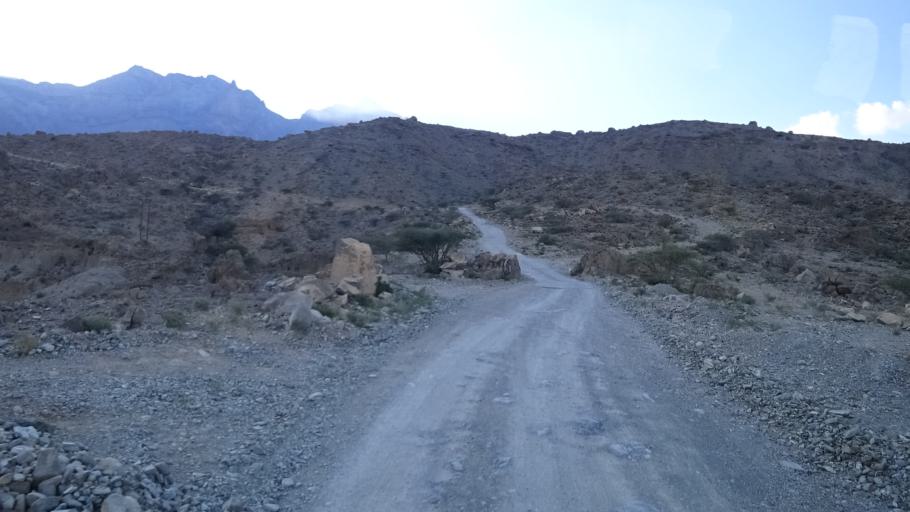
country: OM
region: Al Batinah
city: Rustaq
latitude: 23.2631
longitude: 57.3179
